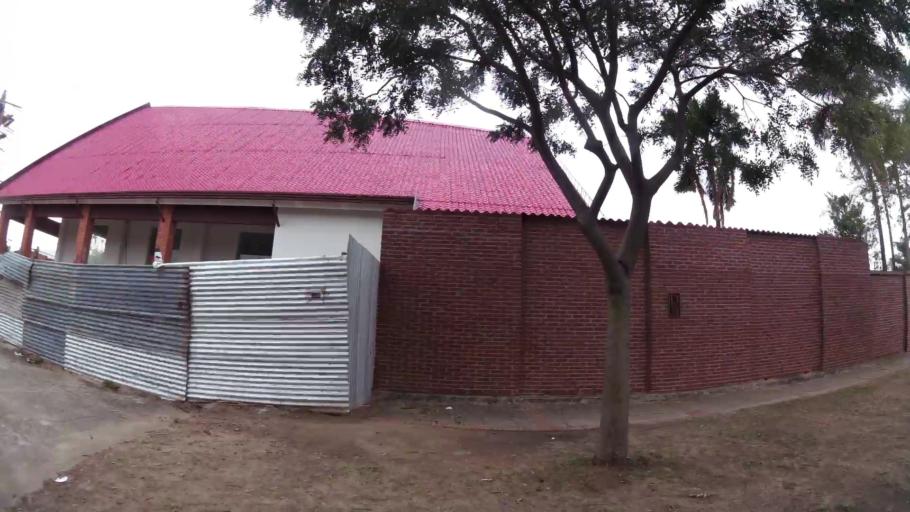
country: BO
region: Santa Cruz
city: Santa Cruz de la Sierra
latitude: -17.7532
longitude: -63.1734
